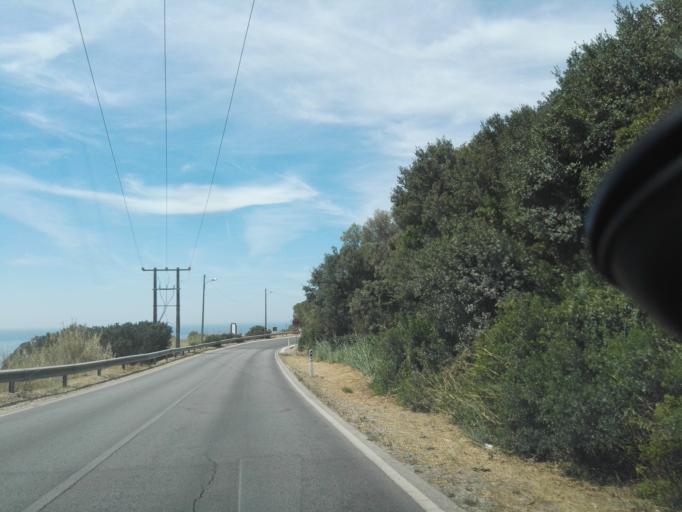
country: PT
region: Setubal
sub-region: Sesimbra
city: Sesimbra
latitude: 38.4412
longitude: -9.0863
